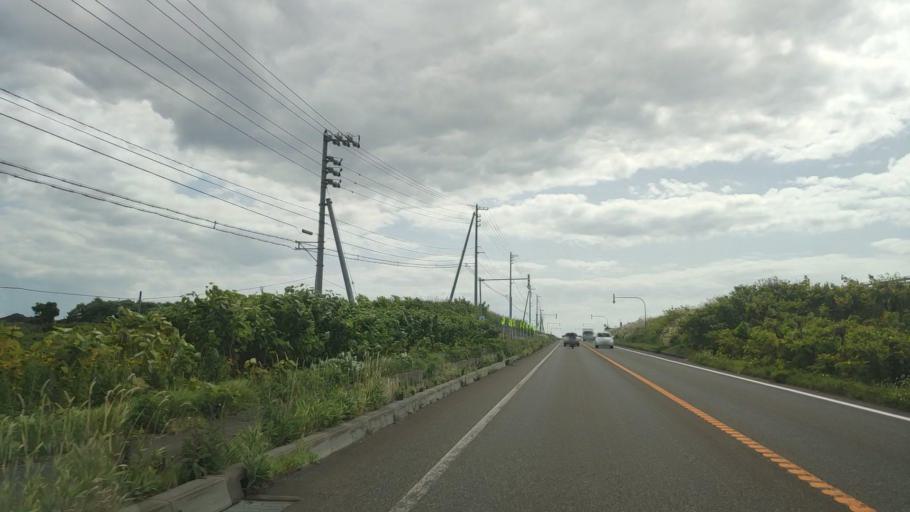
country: JP
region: Hokkaido
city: Rumoi
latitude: 44.5276
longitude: 141.7660
